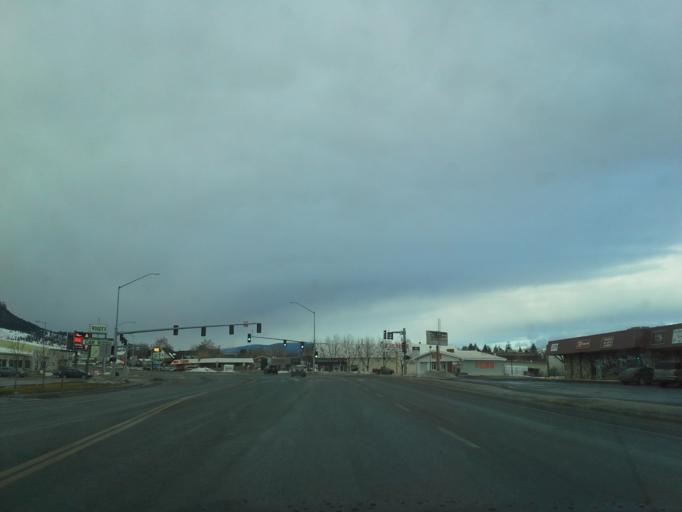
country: US
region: Montana
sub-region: Lewis and Clark County
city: Helena
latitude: 46.6067
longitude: -112.0192
